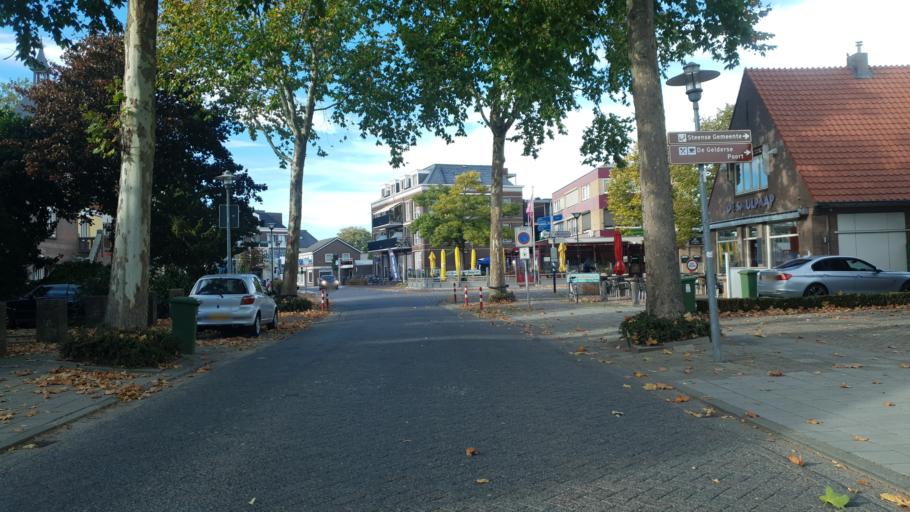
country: NL
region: Gelderland
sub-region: Gemeente Zevenaar
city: Zevenaar
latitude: 51.8634
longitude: 6.0475
